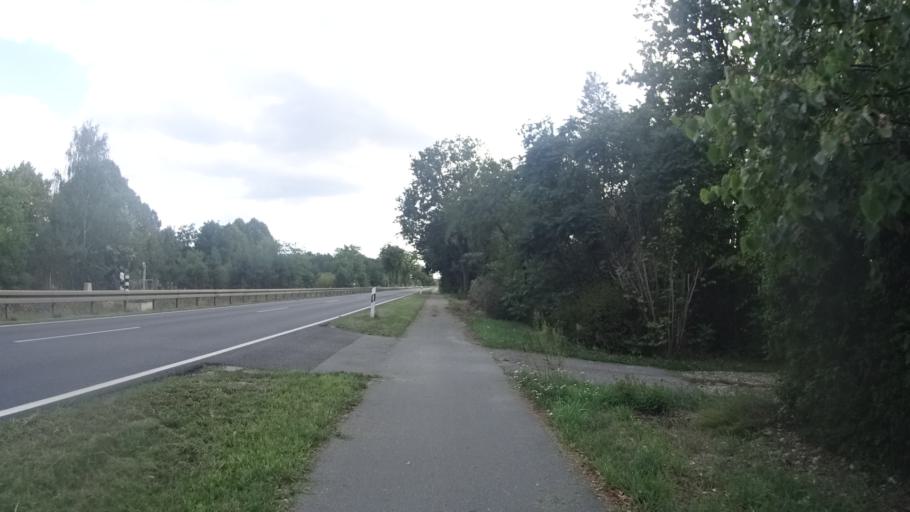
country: DE
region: Brandenburg
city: Rathenow
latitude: 52.5681
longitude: 12.3322
